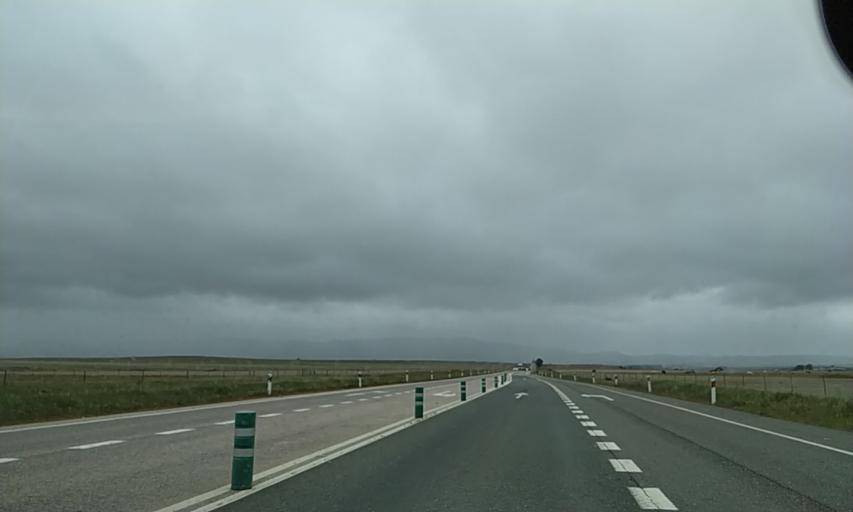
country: ES
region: Extremadura
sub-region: Provincia de Caceres
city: Malpartida de Caceres
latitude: 39.3620
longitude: -6.4628
